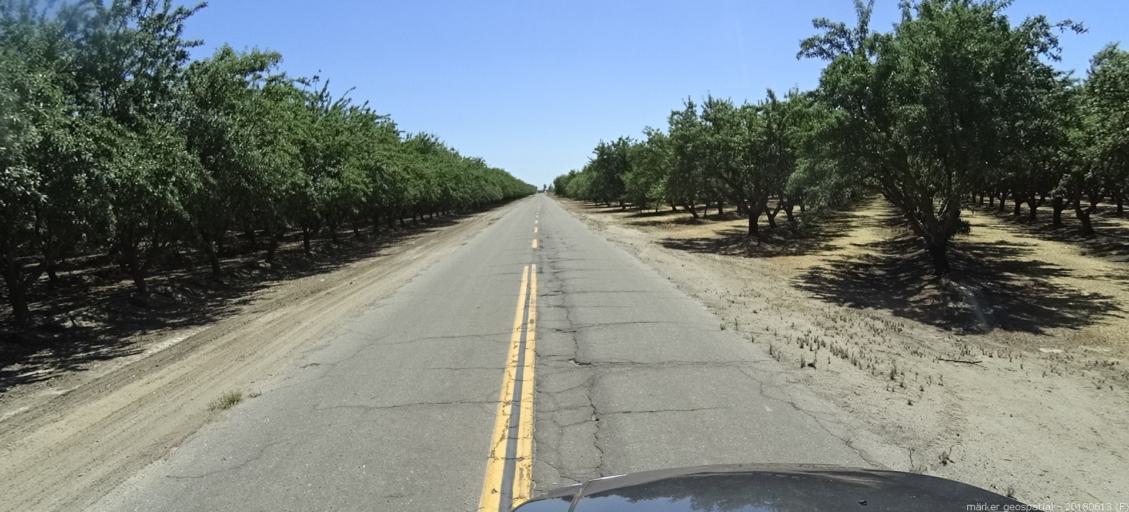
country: US
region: California
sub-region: Madera County
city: Chowchilla
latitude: 37.0399
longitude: -120.3462
